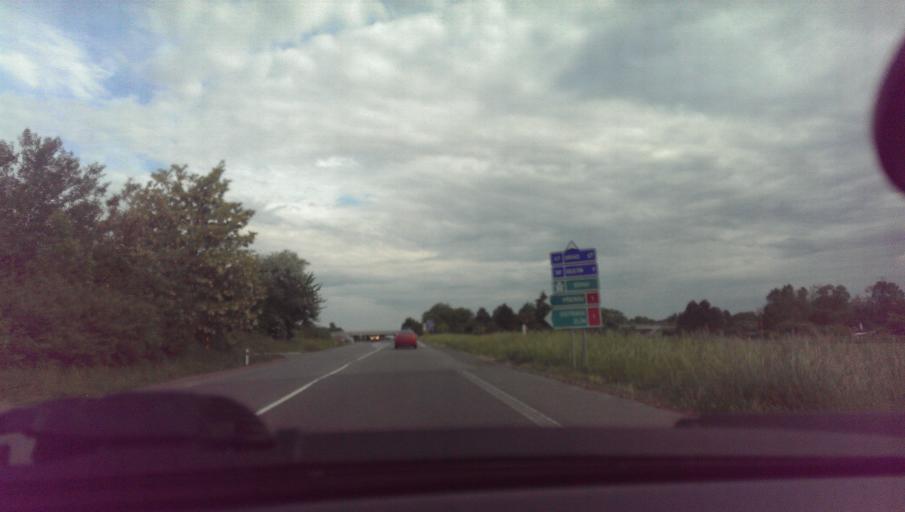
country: CZ
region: Zlin
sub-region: Okres Kromeriz
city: Kromeriz
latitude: 49.3087
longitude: 17.3789
